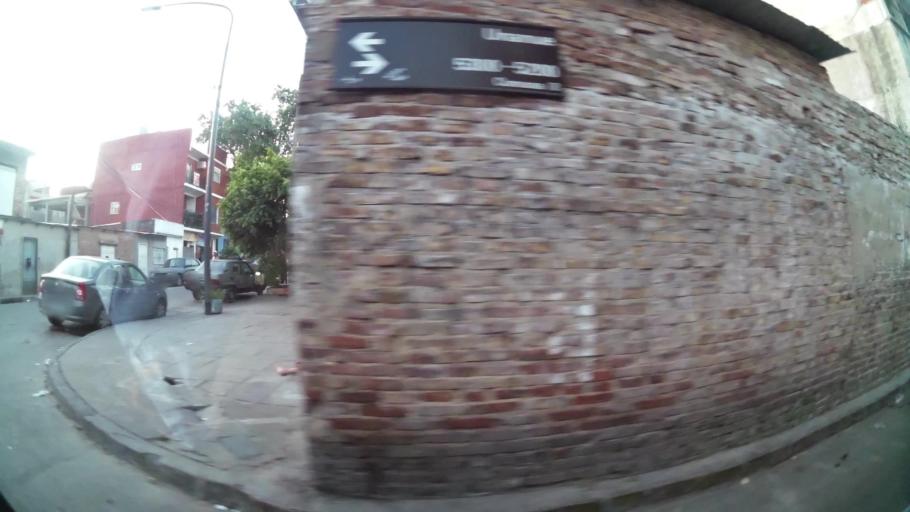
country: AR
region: Buenos Aires F.D.
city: Villa Lugano
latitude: -34.6760
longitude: -58.4686
